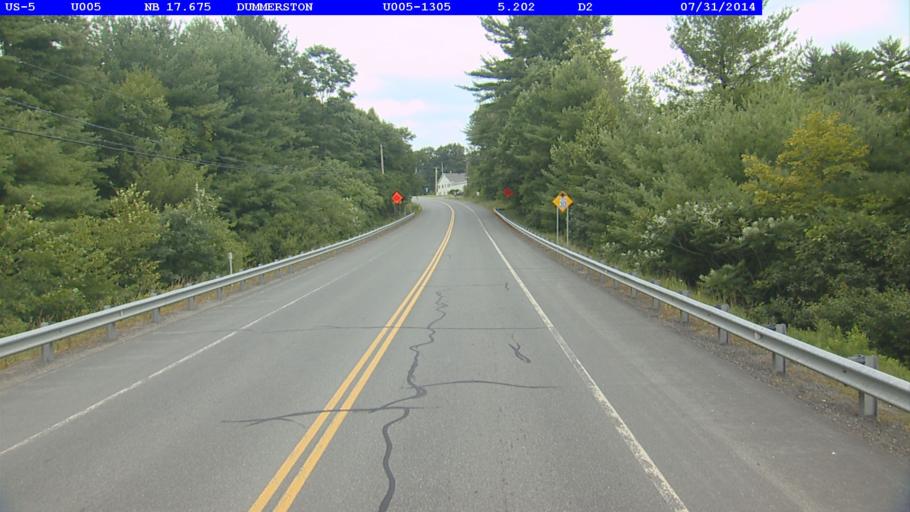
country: US
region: New Hampshire
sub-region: Cheshire County
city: Westmoreland
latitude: 42.9650
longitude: -72.5256
